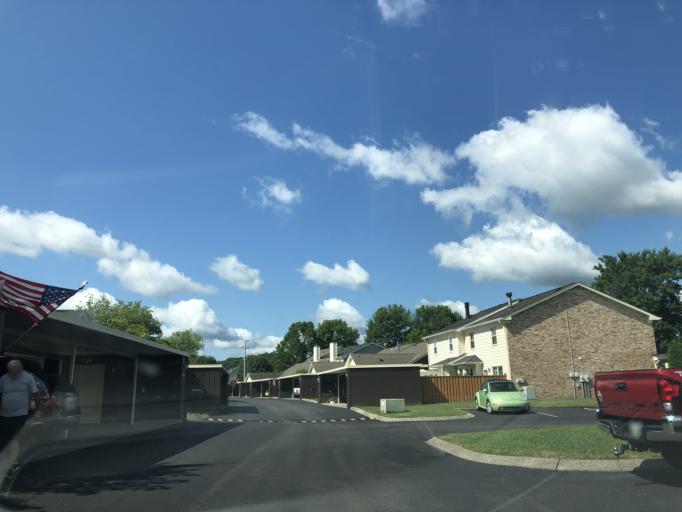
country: US
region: Tennessee
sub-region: Davidson County
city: Belle Meade
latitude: 36.0696
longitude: -86.9501
